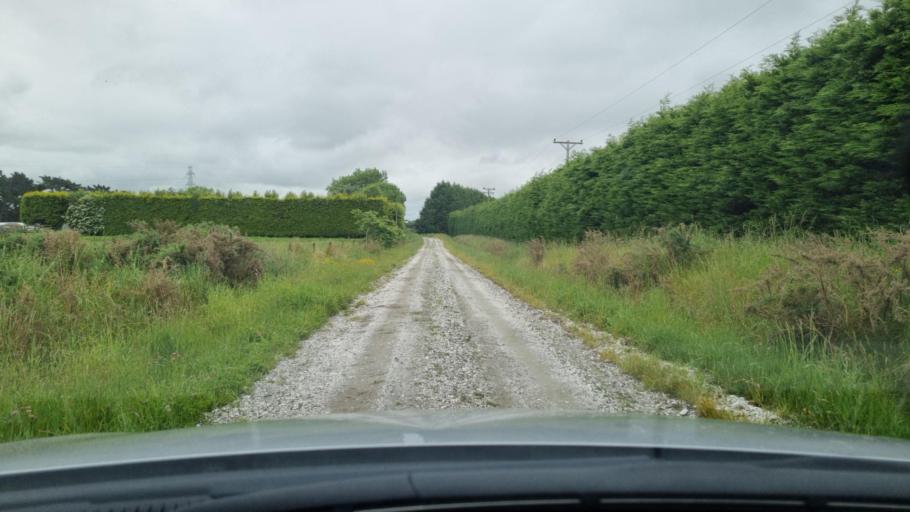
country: NZ
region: Southland
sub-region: Invercargill City
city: Invercargill
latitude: -46.3901
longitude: 168.4046
